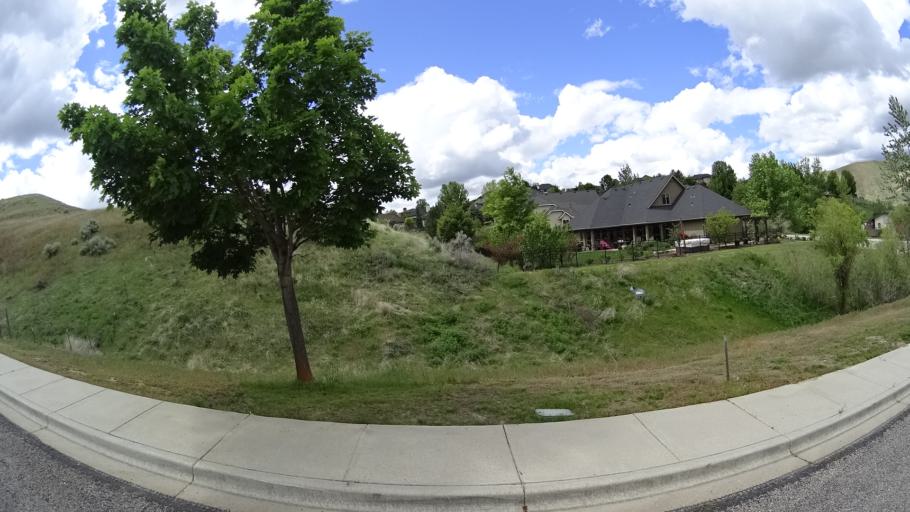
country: US
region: Idaho
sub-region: Ada County
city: Garden City
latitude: 43.6650
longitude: -116.2114
